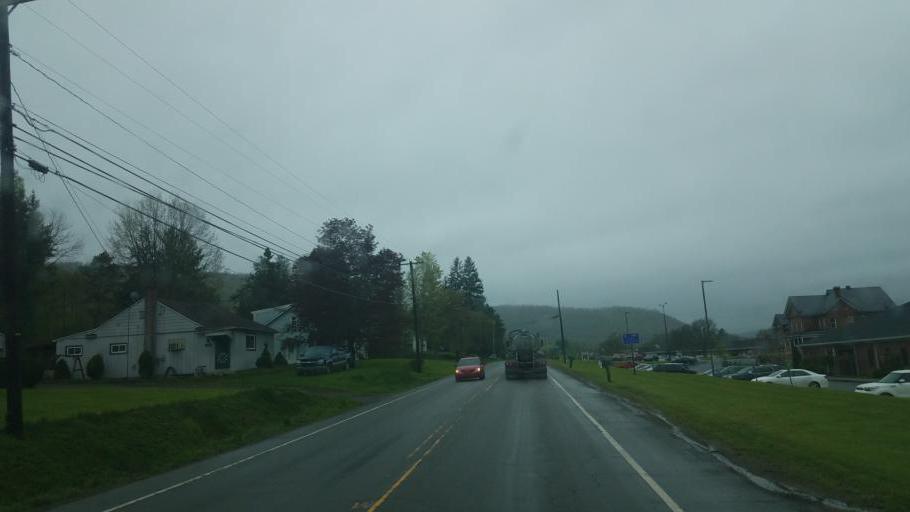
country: US
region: Pennsylvania
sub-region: McKean County
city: Smethport
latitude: 41.7997
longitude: -78.4591
